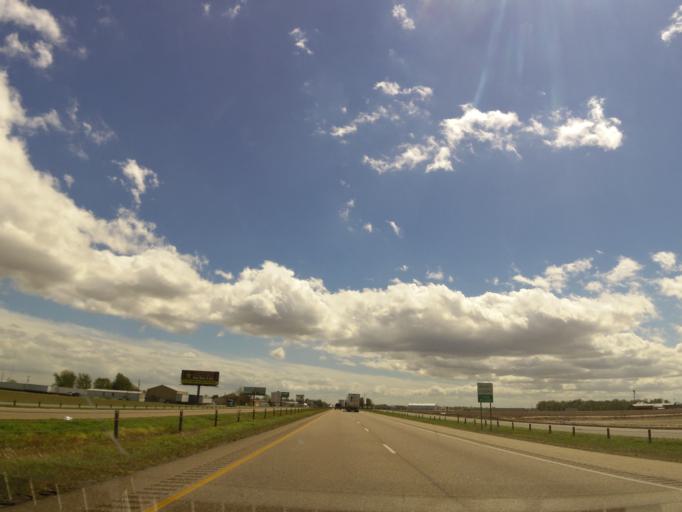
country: US
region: Arkansas
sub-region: Crittenden County
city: Marion
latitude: 35.2415
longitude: -90.2173
